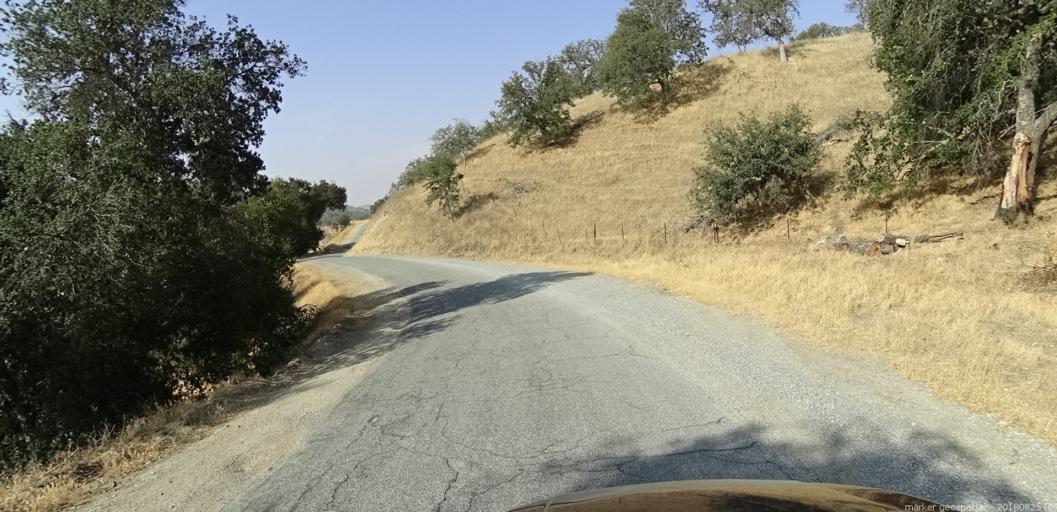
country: US
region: California
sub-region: San Luis Obispo County
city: San Miguel
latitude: 35.8184
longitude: -120.5193
